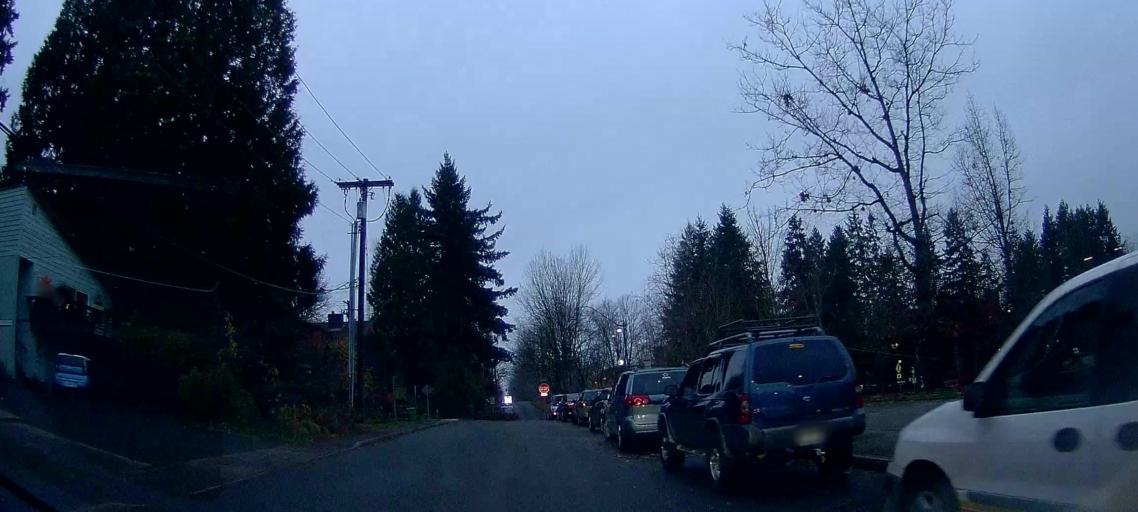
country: US
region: Washington
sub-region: Thurston County
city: Olympia
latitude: 47.0337
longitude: -122.8950
